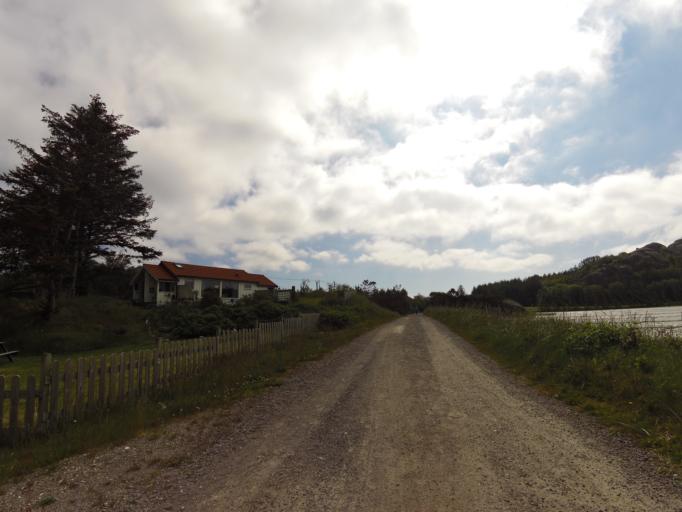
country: NO
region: Rogaland
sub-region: Ha
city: Vigrestad
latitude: 58.5262
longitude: 5.7853
